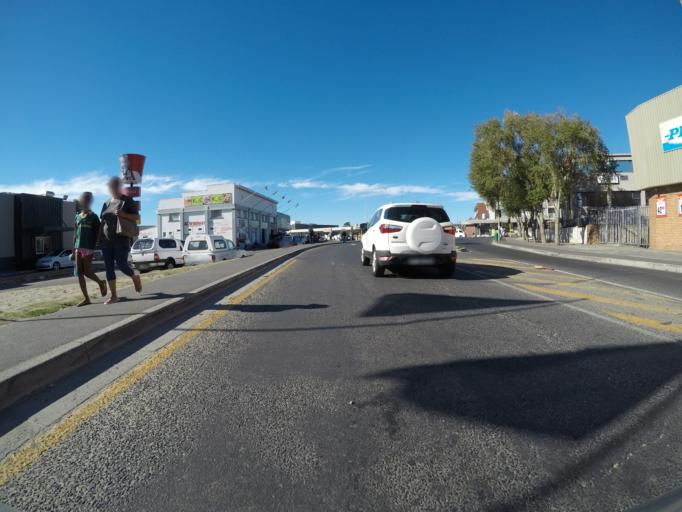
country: ZA
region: Western Cape
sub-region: City of Cape Town
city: Kraaifontein
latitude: -33.9245
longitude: 18.6773
